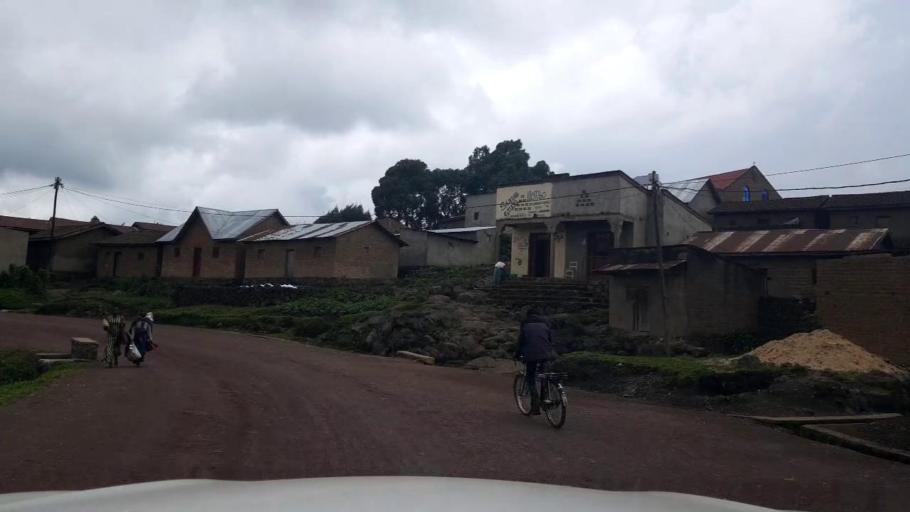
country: RW
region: Northern Province
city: Musanze
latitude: -1.5818
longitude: 29.4751
